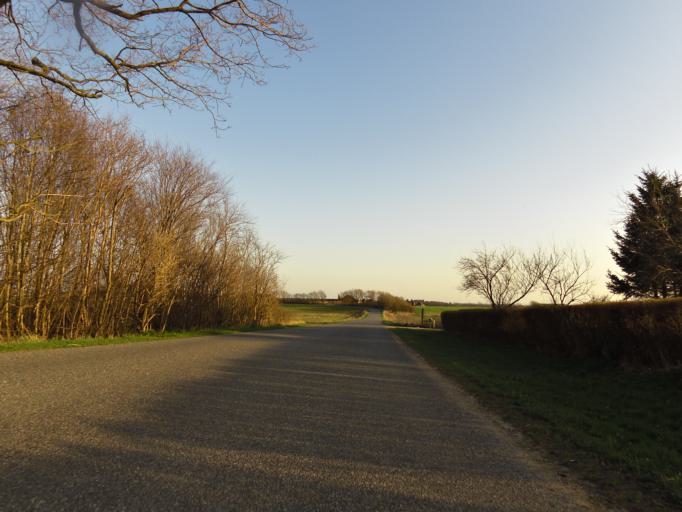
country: DK
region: Central Jutland
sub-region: Holstebro Kommune
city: Vinderup
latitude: 56.5169
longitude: 8.7947
